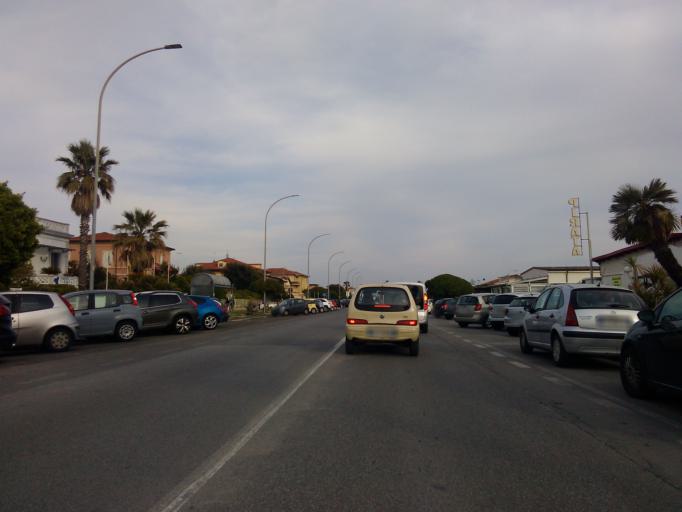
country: IT
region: Tuscany
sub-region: Provincia di Massa-Carrara
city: Massa
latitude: 44.0061
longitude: 10.1017
